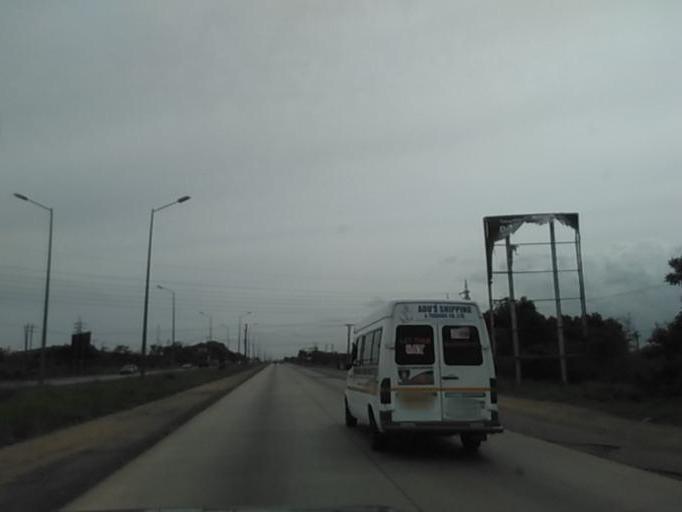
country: GH
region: Greater Accra
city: Nungua
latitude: 5.6500
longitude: -0.1062
